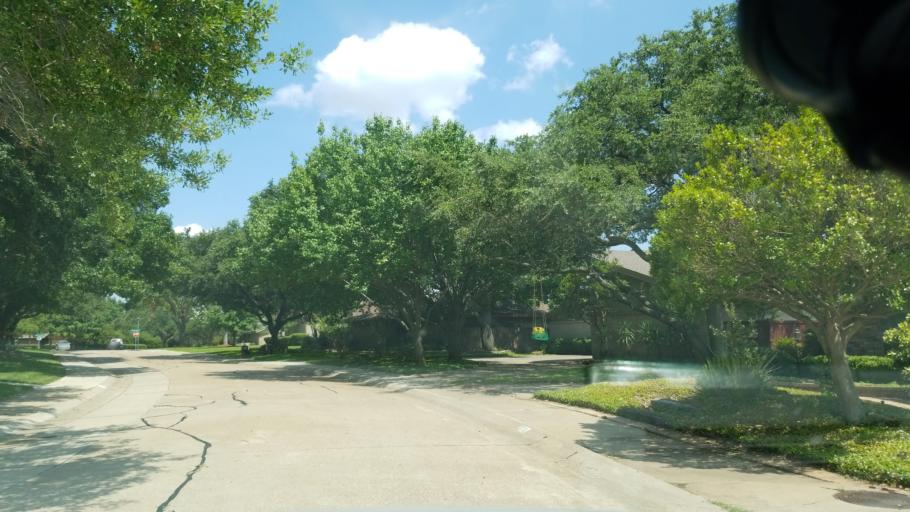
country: US
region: Texas
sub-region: Dallas County
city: Carrollton
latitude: 32.9622
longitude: -96.8625
